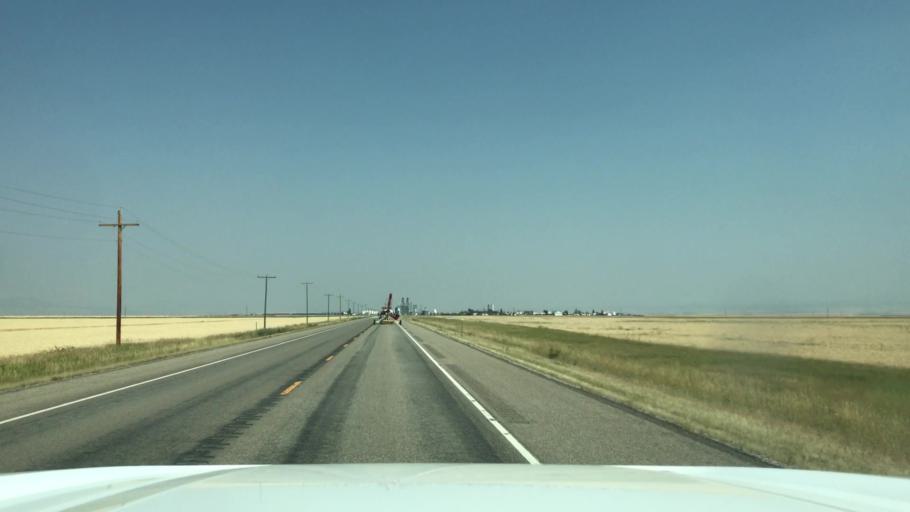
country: US
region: Montana
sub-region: Judith Basin County
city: Stanford
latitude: 47.0552
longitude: -109.9349
